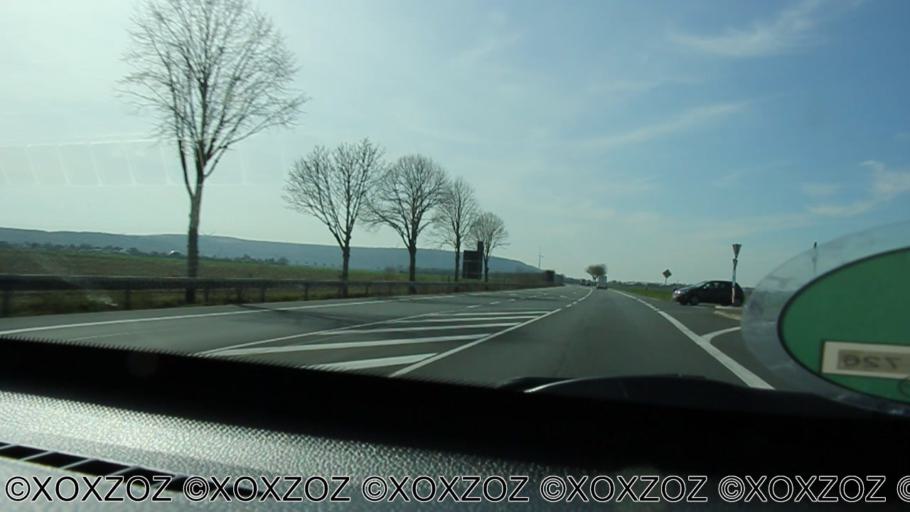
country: DE
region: North Rhine-Westphalia
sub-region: Regierungsbezirk Koln
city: Elsdorf
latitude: 50.9535
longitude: 6.5383
